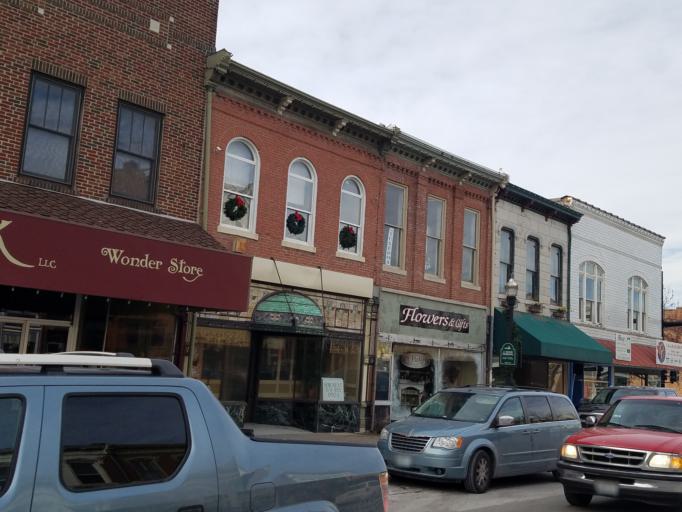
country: US
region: Missouri
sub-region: Cooper County
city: Boonville
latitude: 38.9759
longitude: -92.7438
